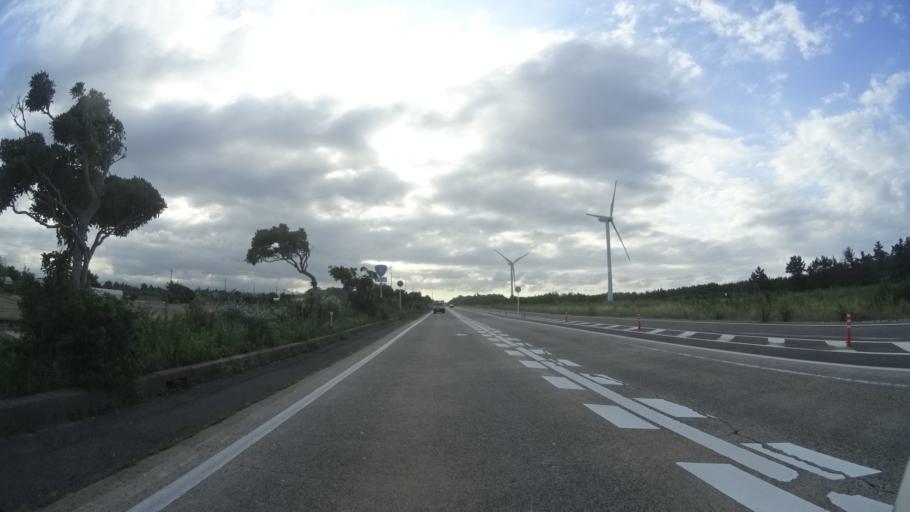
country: JP
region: Tottori
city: Kurayoshi
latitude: 35.4985
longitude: 133.8000
